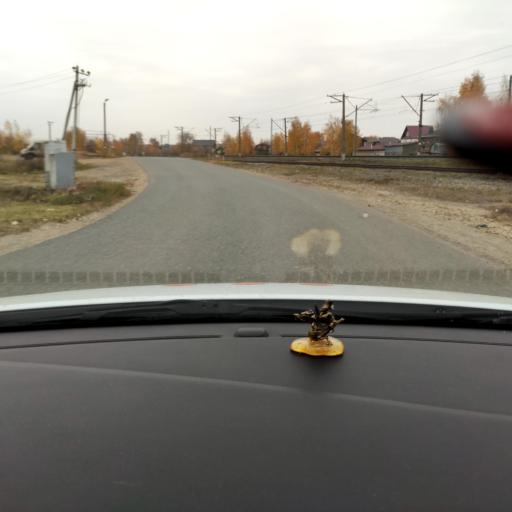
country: RU
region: Tatarstan
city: Verkhniy Uslon
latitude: 55.8018
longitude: 49.0246
